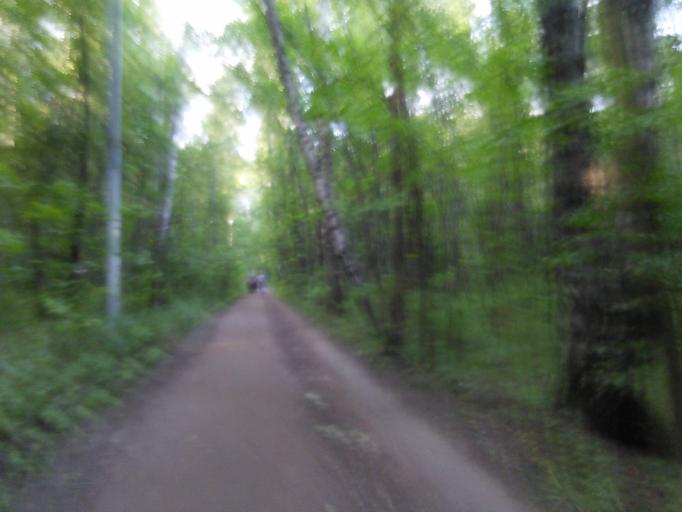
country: RU
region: Moscow
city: Sokol'niki
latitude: 55.8052
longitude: 37.6753
